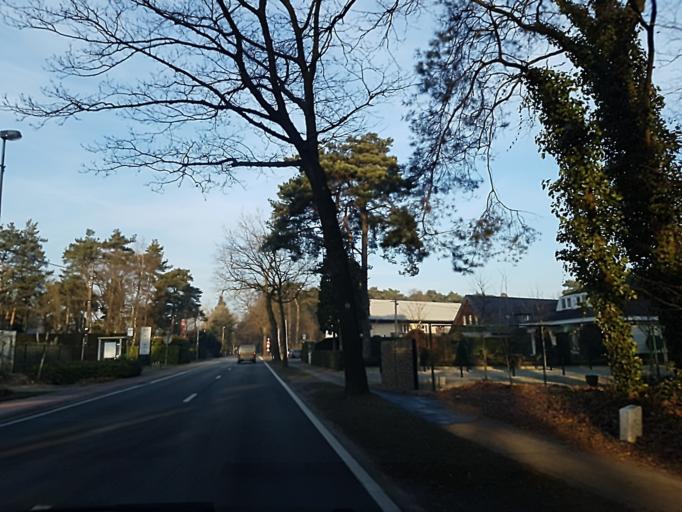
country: BE
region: Flanders
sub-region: Provincie Antwerpen
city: Zoersel
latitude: 51.2779
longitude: 4.7181
